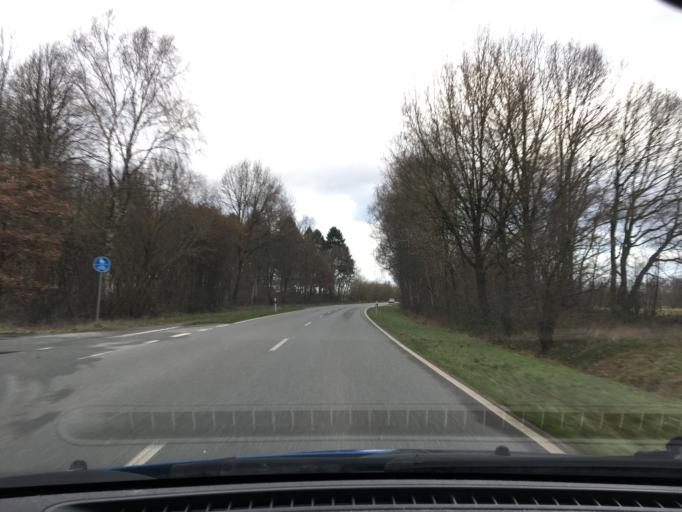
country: DE
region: Schleswig-Holstein
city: Kaisborstel
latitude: 54.0232
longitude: 9.4757
